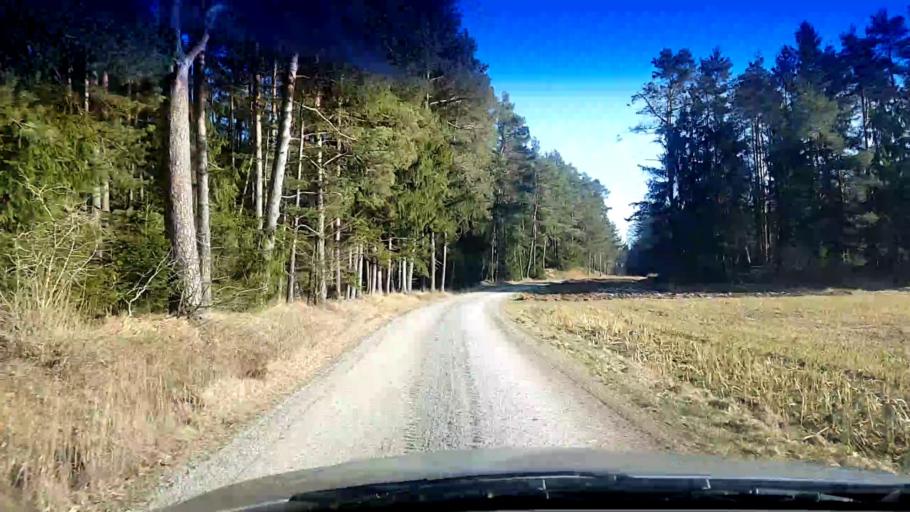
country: DE
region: Bavaria
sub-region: Upper Franconia
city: Aufsess
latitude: 49.9202
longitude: 11.2011
